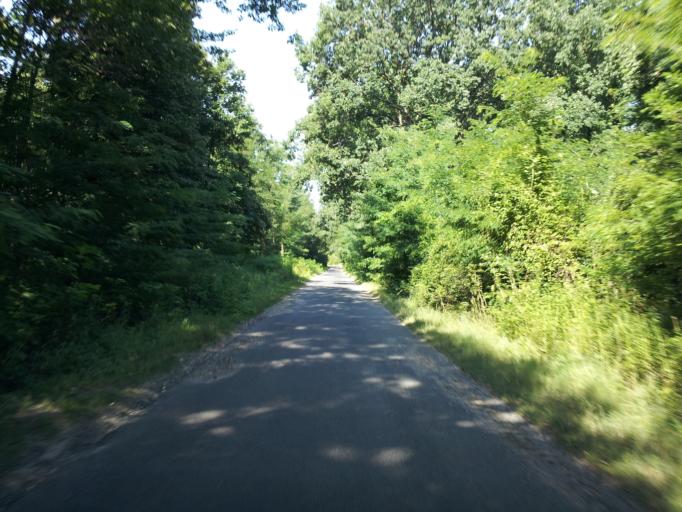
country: HU
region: Zala
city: Cserszegtomaj
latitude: 46.8458
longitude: 17.2007
